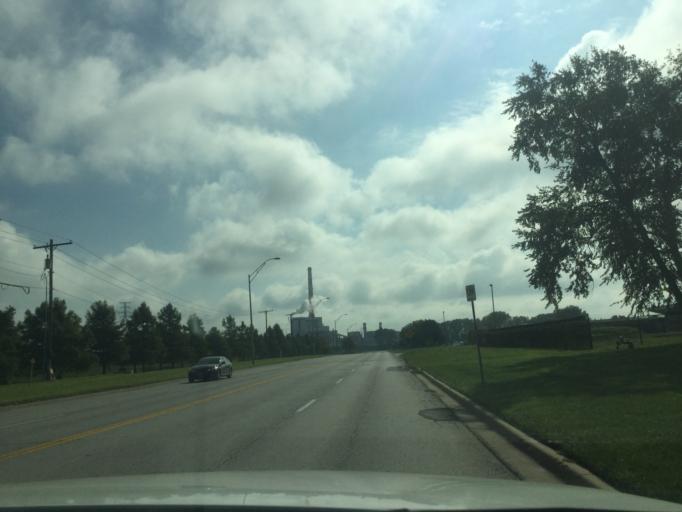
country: US
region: Missouri
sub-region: Jackson County
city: Sugar Creek
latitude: 39.1299
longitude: -94.4931
